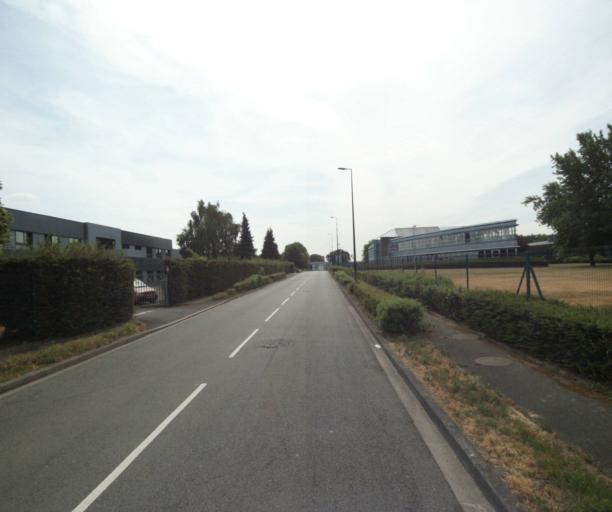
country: FR
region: Nord-Pas-de-Calais
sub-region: Departement du Nord
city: Mouvaux
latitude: 50.7177
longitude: 3.1285
